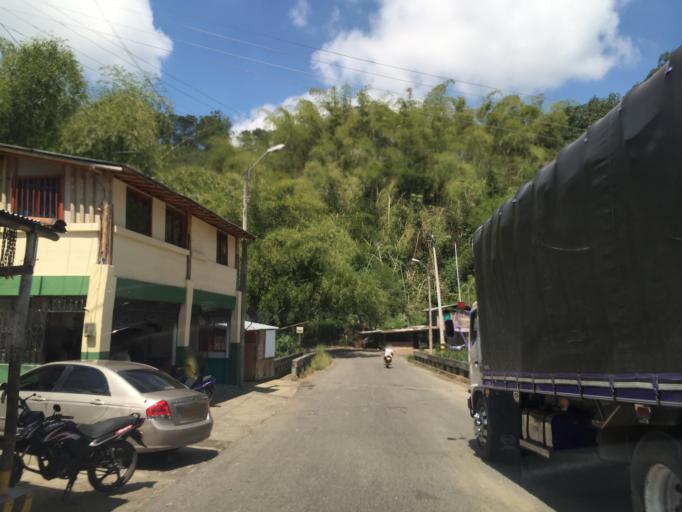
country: CO
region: Valle del Cauca
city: Alcala
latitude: 4.7190
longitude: -75.7939
